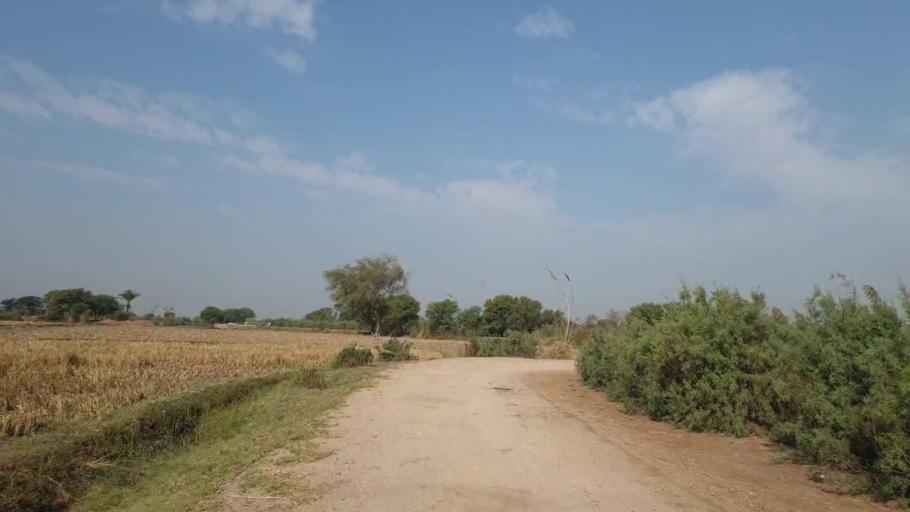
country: PK
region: Sindh
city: Tando Muhammad Khan
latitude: 25.0711
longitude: 68.4339
